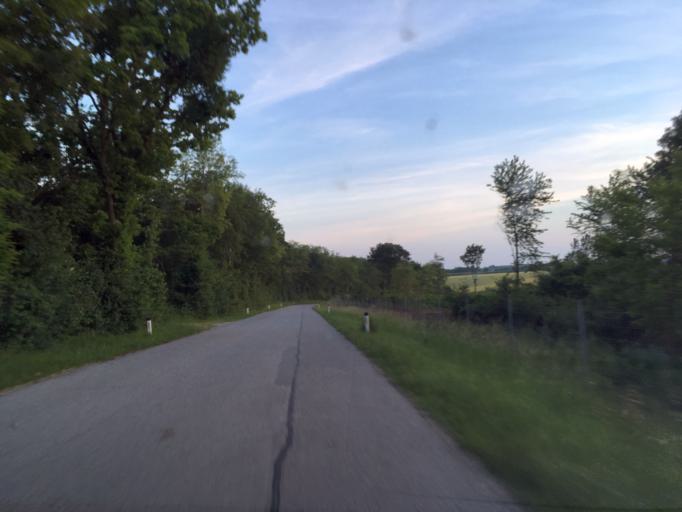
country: AT
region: Lower Austria
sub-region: Politischer Bezirk Mistelbach
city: Herrnbaumgarten
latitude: 48.7149
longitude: 16.6690
